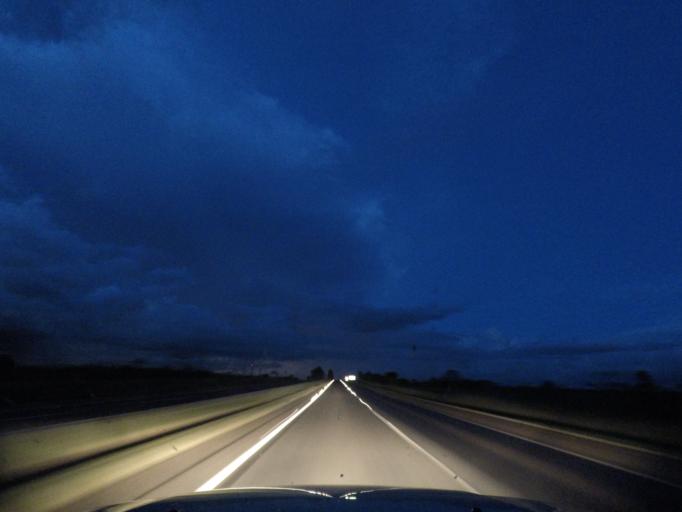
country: BR
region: Minas Gerais
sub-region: Uberlandia
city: Uberlandia
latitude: -19.1987
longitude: -48.1521
